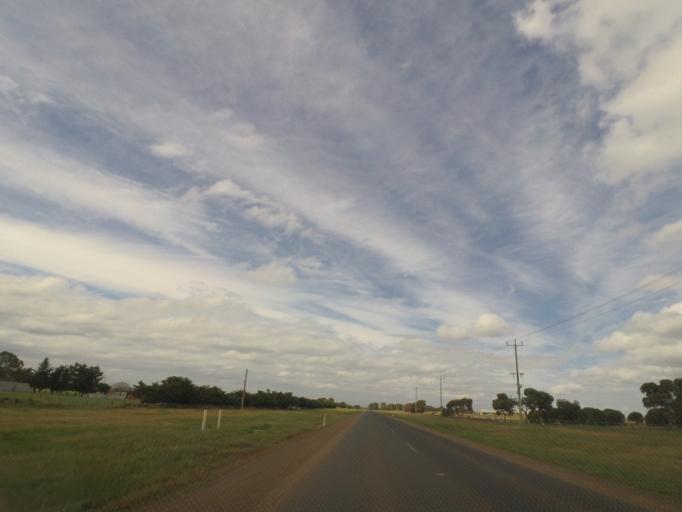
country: AU
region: Victoria
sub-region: Melton
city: Rockbank
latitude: -37.7453
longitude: 144.6363
